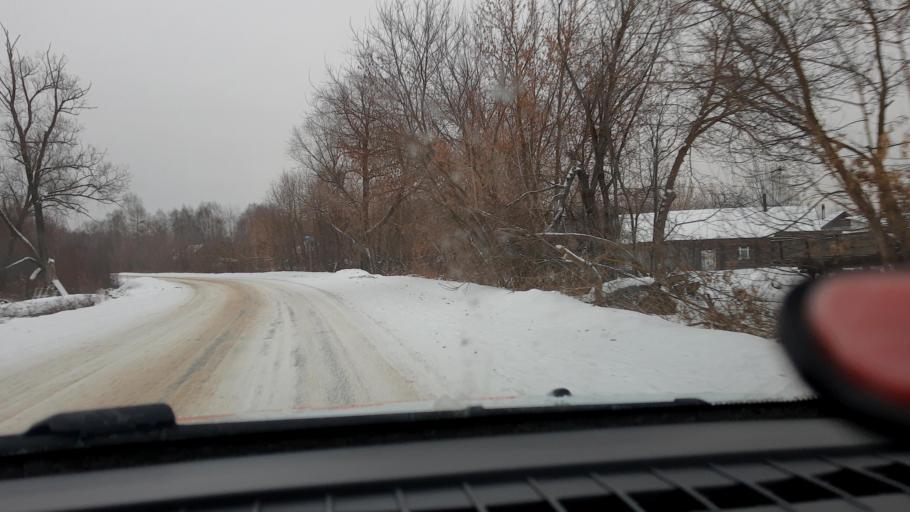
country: RU
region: Nizjnij Novgorod
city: Pamyat' Parizhskoy Kommuny
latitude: 56.2393
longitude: 44.5363
